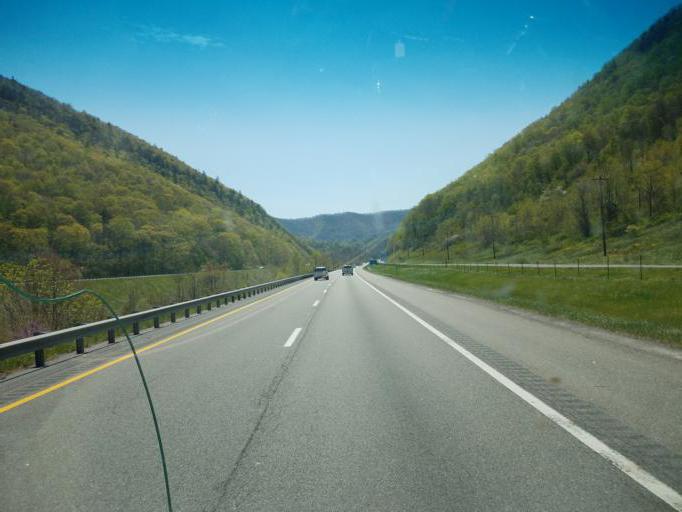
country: US
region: Virginia
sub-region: Bland County
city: Bland
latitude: 37.2285
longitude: -81.0954
